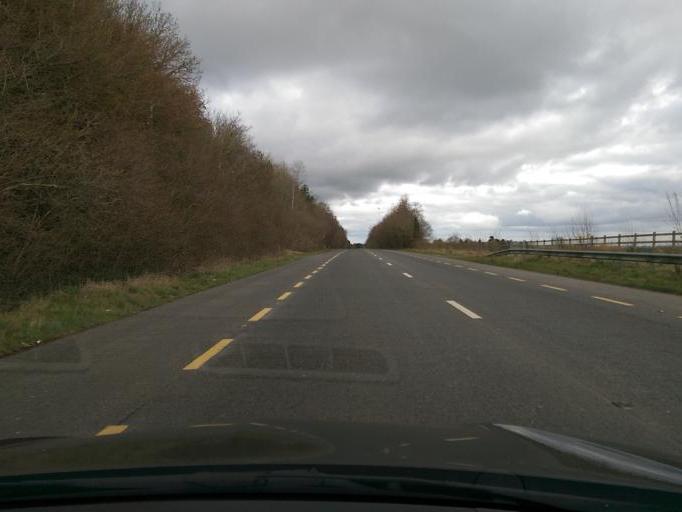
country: IE
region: Leinster
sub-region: An Iarmhi
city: Moate
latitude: 53.3908
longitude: -7.7665
